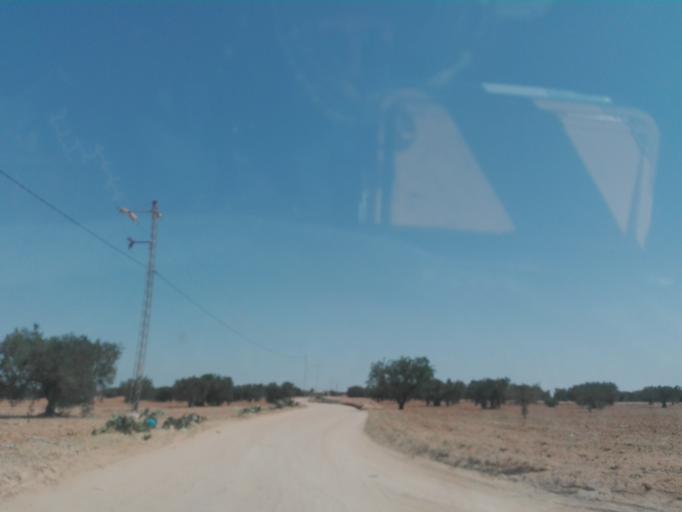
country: TN
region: Safaqis
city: Bi'r `Ali Bin Khalifah
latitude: 34.6703
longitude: 10.2355
